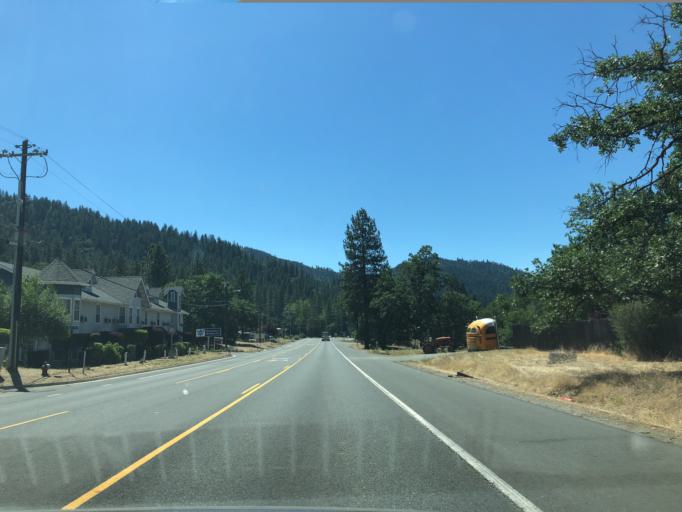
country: US
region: California
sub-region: Trinity County
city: Weaverville
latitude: 40.7161
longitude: -122.9262
